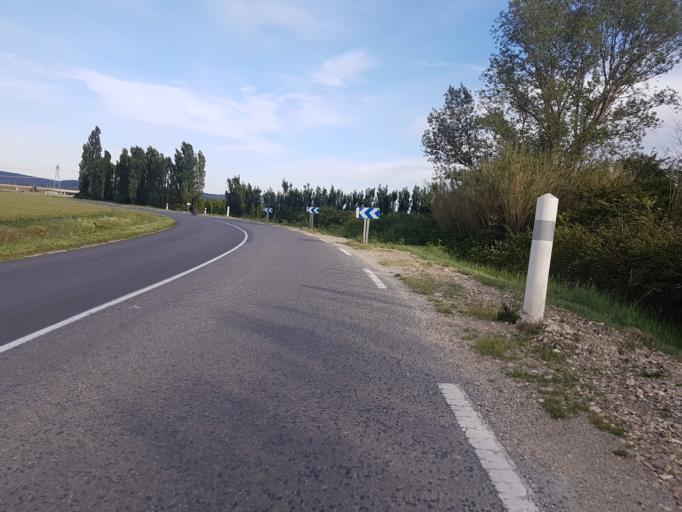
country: FR
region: Languedoc-Roussillon
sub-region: Departement du Gard
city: Pont-Saint-Esprit
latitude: 44.2557
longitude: 4.6807
